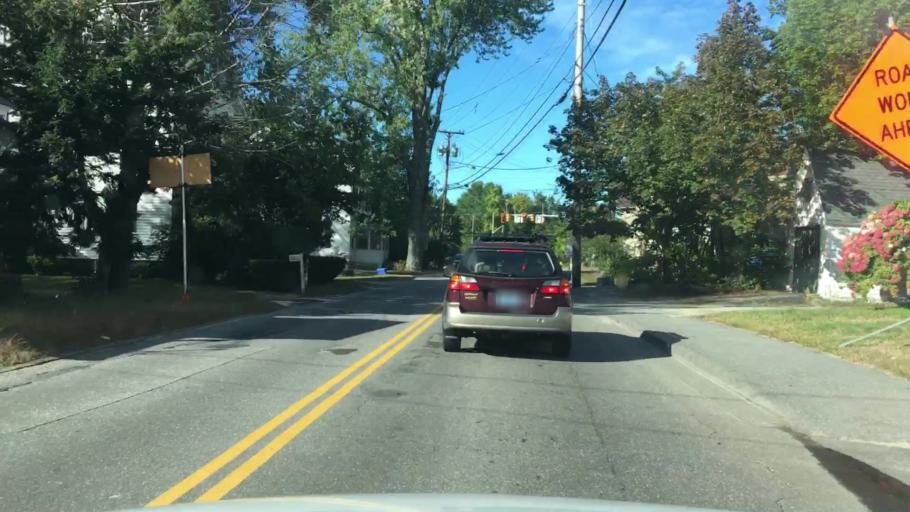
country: US
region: Maine
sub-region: Cumberland County
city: Brunswick
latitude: 43.9118
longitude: -69.9762
